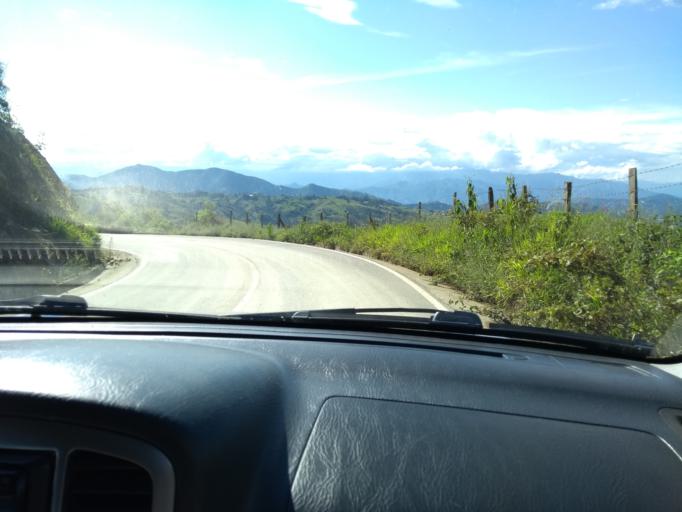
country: CO
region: Caldas
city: Salamina
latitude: 5.3754
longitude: -75.4520
